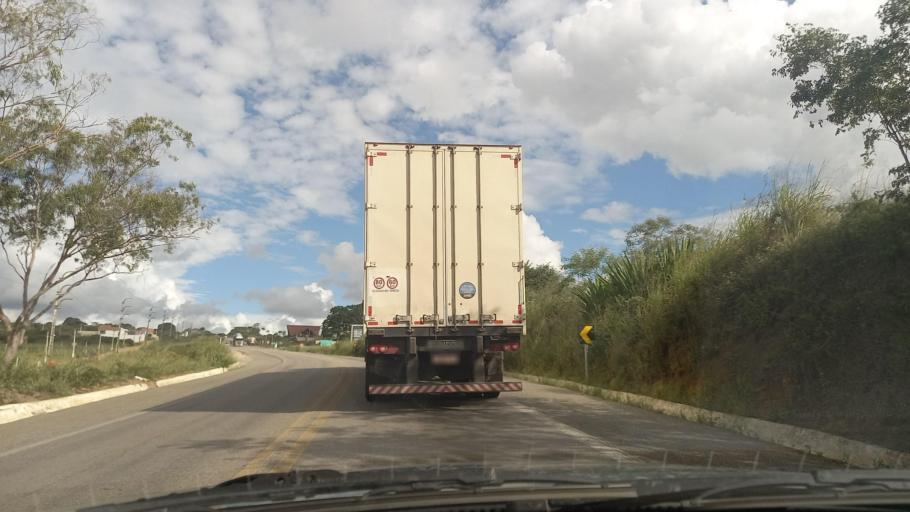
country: BR
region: Pernambuco
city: Garanhuns
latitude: -8.8593
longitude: -36.4647
